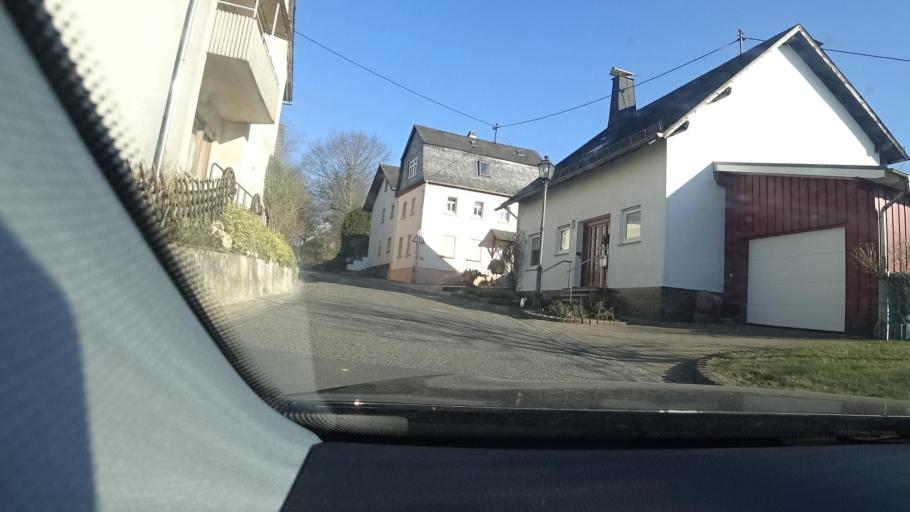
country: DE
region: Rheinland-Pfalz
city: Mutterschied
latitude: 49.9815
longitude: 7.5681
